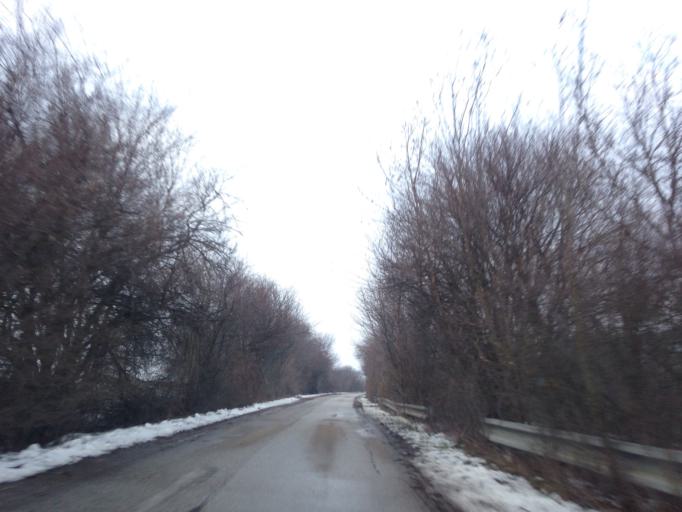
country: SK
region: Nitriansky
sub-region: Okres Nitra
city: Vrable
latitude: 48.0798
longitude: 18.3704
